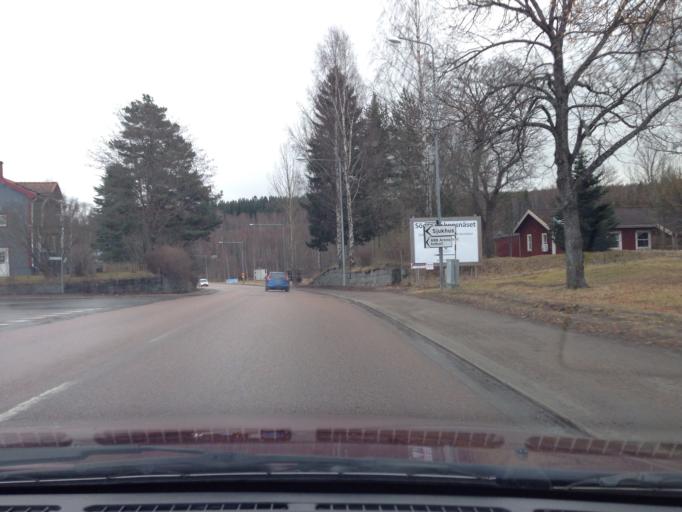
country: SE
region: Dalarna
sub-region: Ludvika Kommun
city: Ludvika
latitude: 60.1490
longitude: 15.2108
